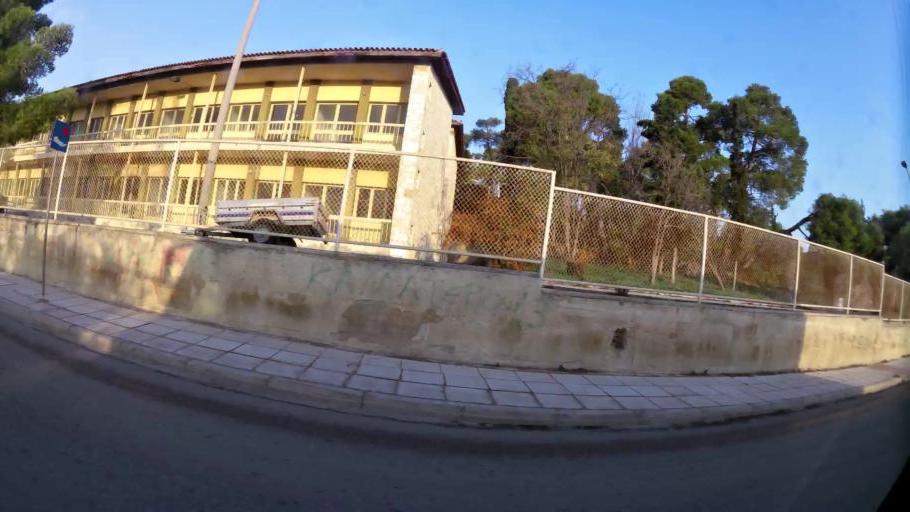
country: GR
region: Attica
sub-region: Nomarchia Athinas
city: Kamateron
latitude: 38.0494
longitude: 23.7189
